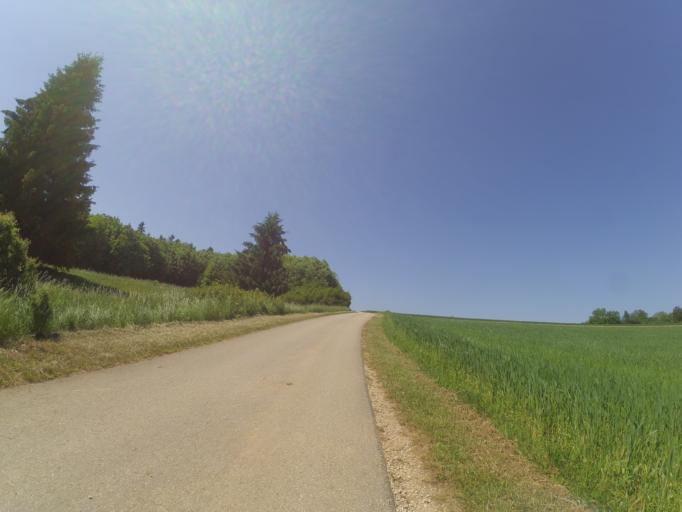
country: DE
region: Baden-Wuerttemberg
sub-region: Tuebingen Region
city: Merklingen
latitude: 48.4985
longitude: 9.7827
